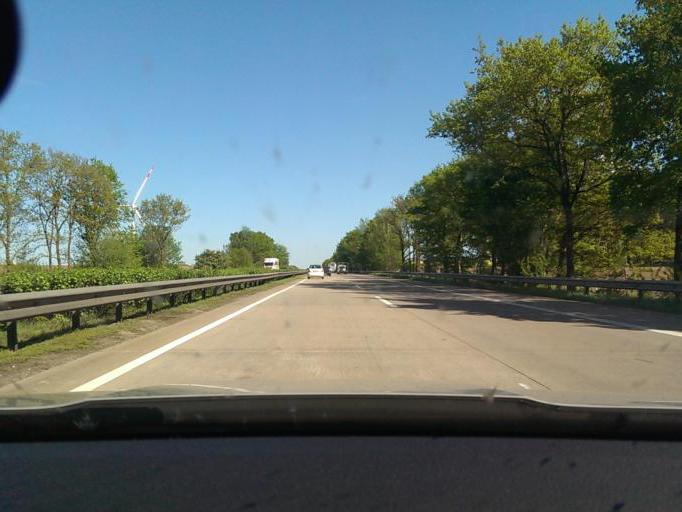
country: DE
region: Lower Saxony
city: Hauslingen
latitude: 52.8858
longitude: 9.4574
